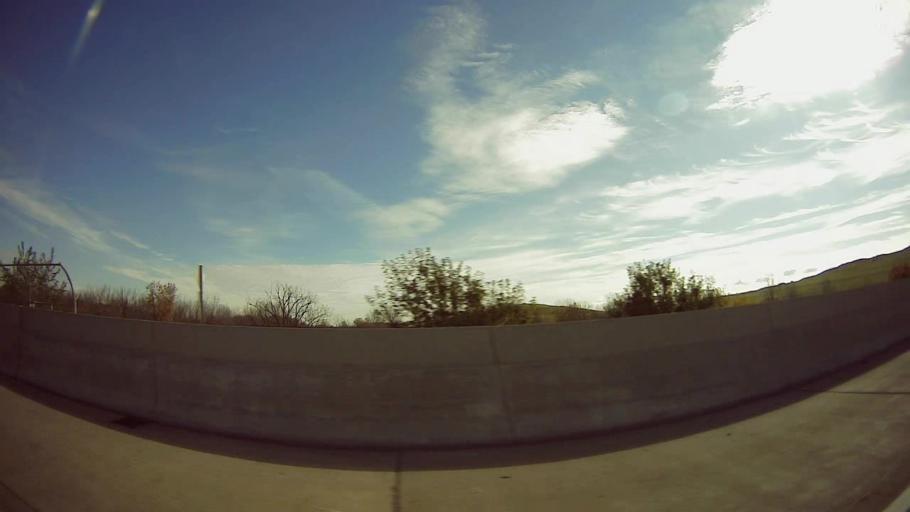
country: US
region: Michigan
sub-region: Wayne County
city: Wayne
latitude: 42.2685
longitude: -83.4406
